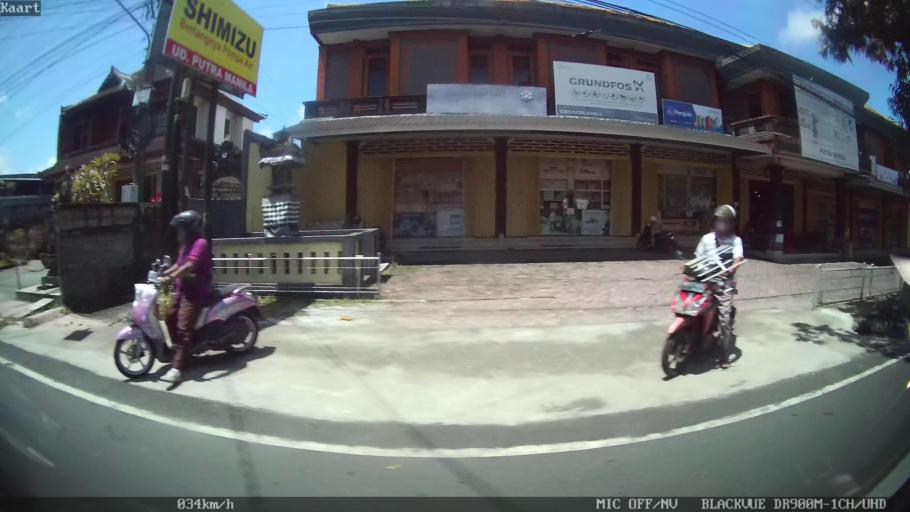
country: ID
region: Bali
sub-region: Kabupaten Gianyar
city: Ubud
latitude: -8.5520
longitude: 115.3031
